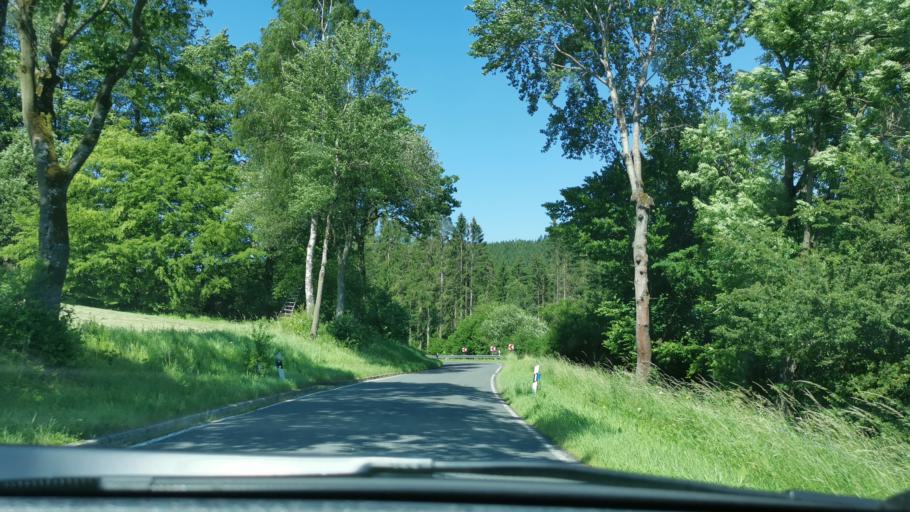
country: DE
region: Hesse
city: Hessisch Lichtenau
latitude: 51.1610
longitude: 9.7582
